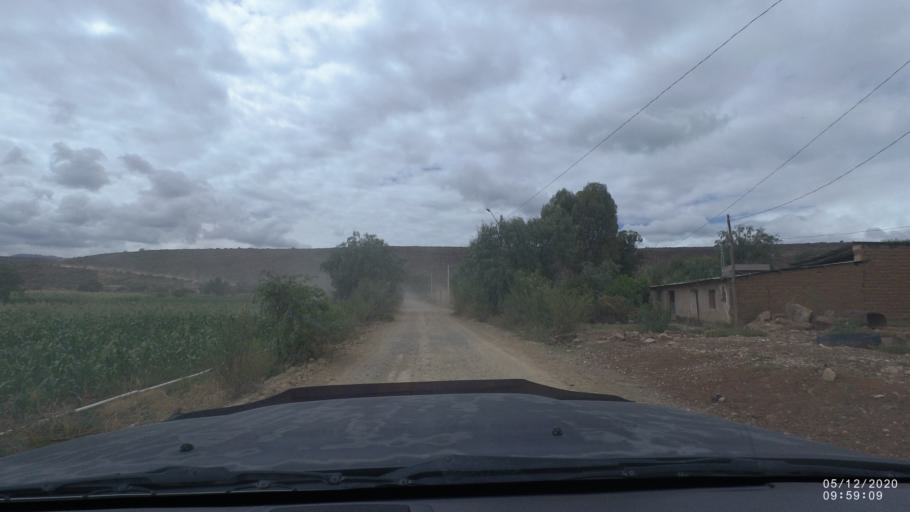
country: BO
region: Cochabamba
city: Sipe Sipe
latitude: -17.4337
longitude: -66.2917
